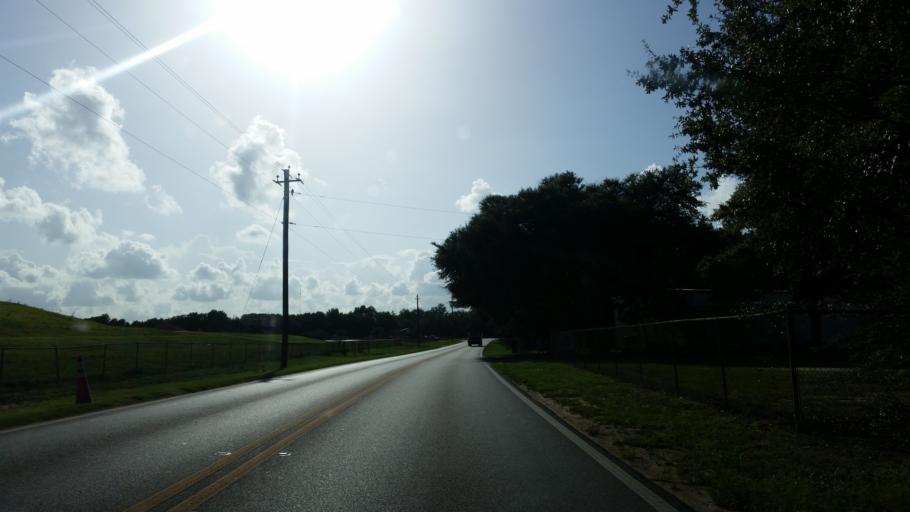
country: US
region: Florida
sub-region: Santa Rosa County
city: Bagdad
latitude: 30.5829
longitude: -87.0573
